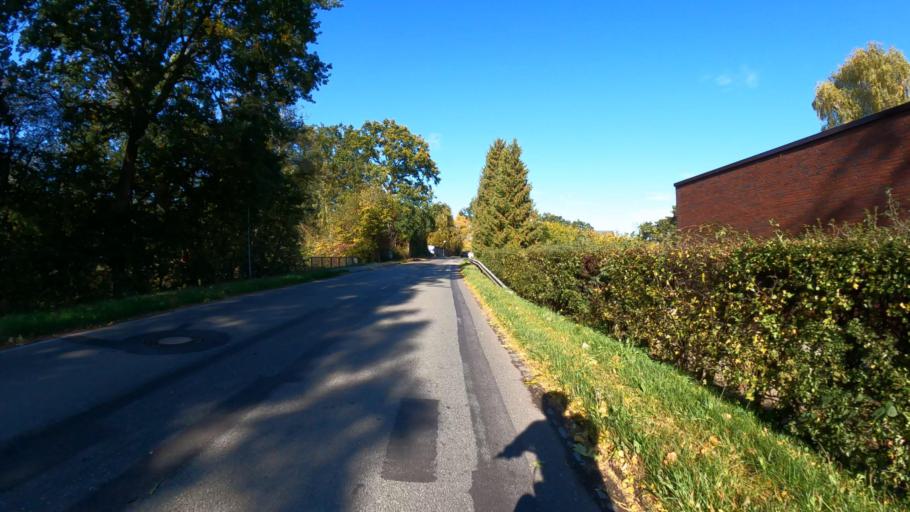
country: DE
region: Schleswig-Holstein
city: Ahrensburg
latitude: 53.6885
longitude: 10.2254
